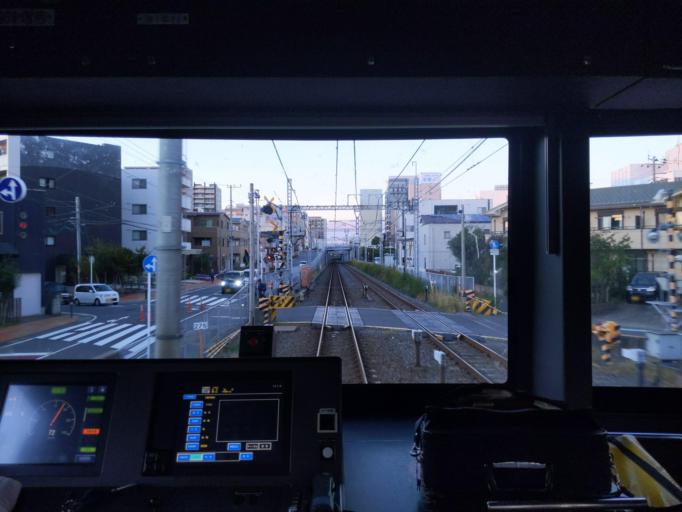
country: JP
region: Chiba
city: Shiroi
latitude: 35.7751
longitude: 139.9996
